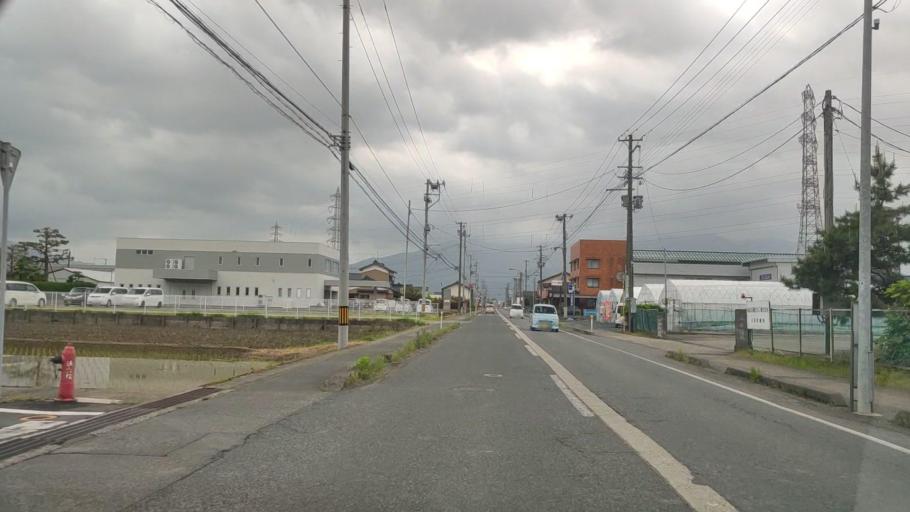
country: JP
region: Niigata
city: Gosen
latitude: 37.7346
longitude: 139.1945
